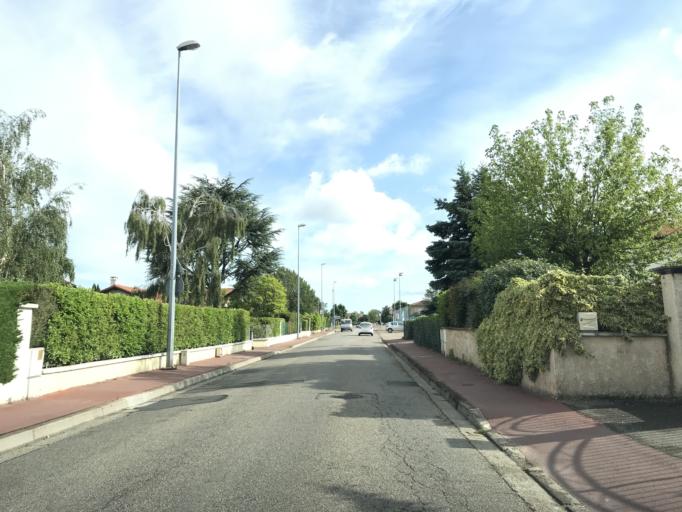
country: FR
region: Rhone-Alpes
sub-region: Departement du Rhone
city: Mions
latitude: 45.6620
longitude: 4.9492
